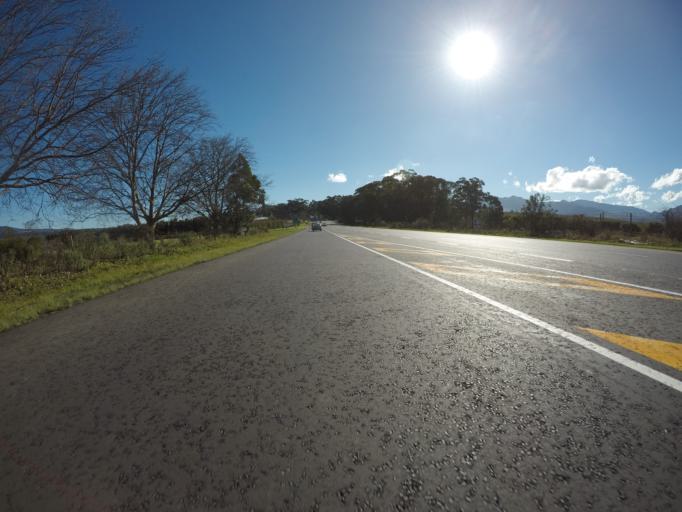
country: ZA
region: Western Cape
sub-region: Overberg District Municipality
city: Grabouw
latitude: -34.1658
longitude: 19.0381
